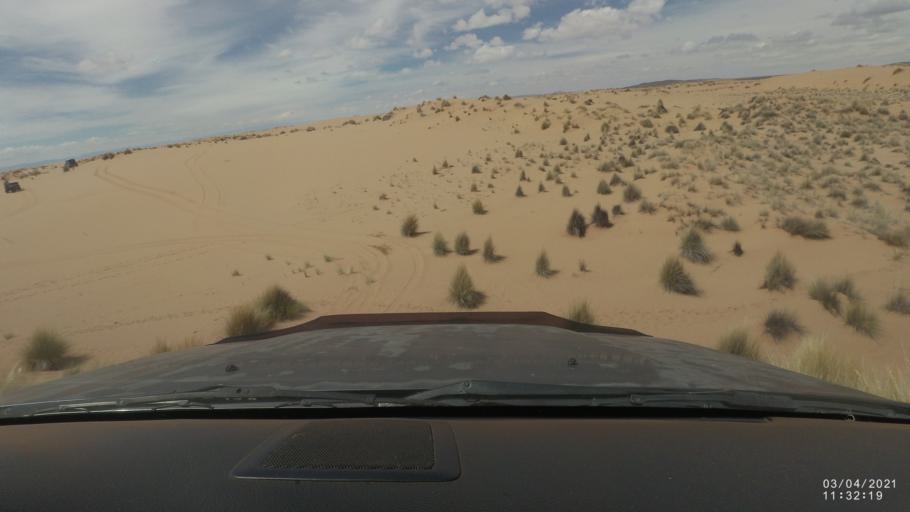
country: BO
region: Oruro
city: Poopo
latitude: -18.7024
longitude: -67.5073
